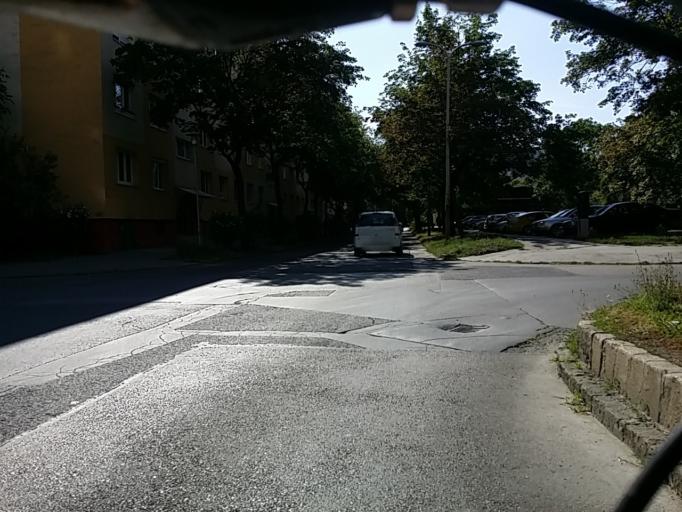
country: HU
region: Budapest
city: Budapest III. keruelet
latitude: 47.5460
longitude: 19.0400
